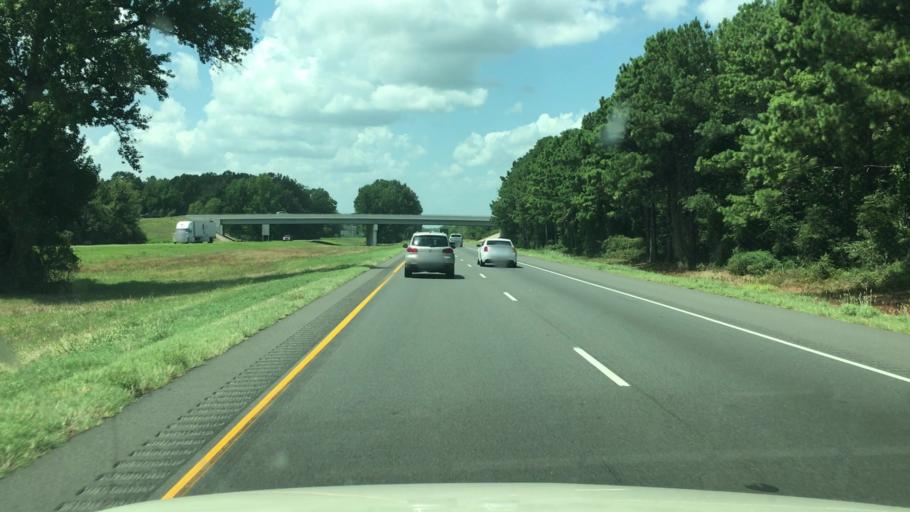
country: US
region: Arkansas
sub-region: Hempstead County
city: Hope
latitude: 33.6839
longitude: -93.6083
